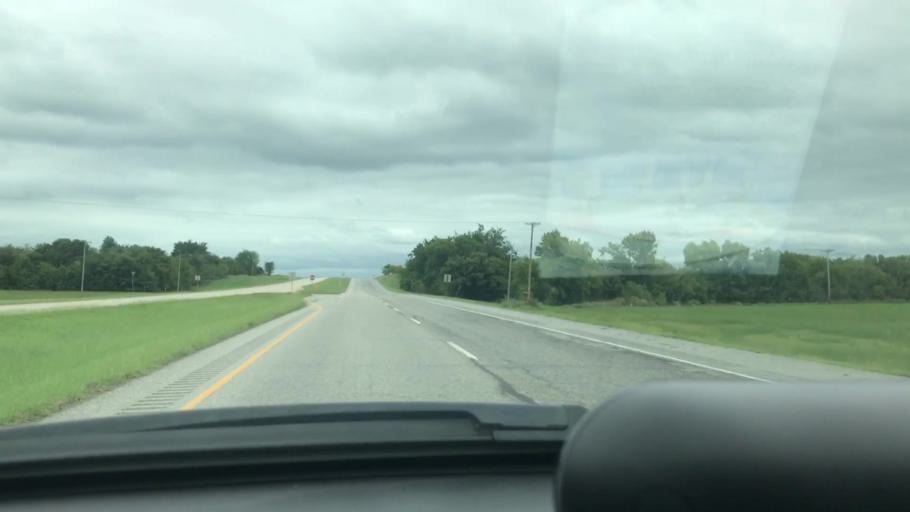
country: US
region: Oklahoma
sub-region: Wagoner County
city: Wagoner
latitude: 35.9872
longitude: -95.3751
